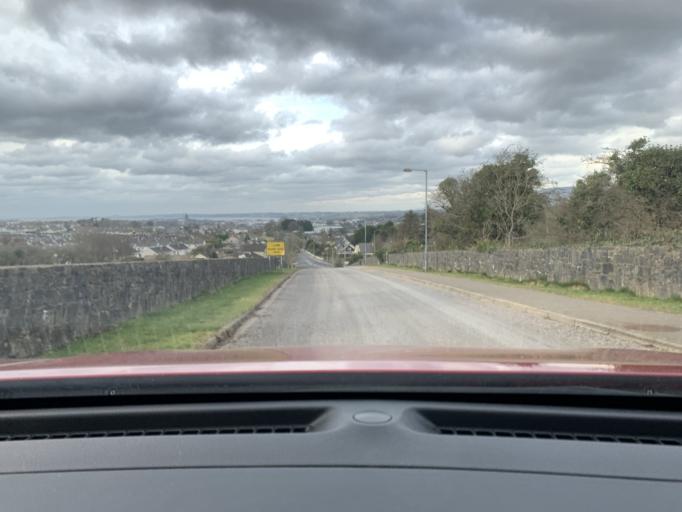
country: IE
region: Connaught
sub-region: Sligo
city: Sligo
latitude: 54.2573
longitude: -8.4559
